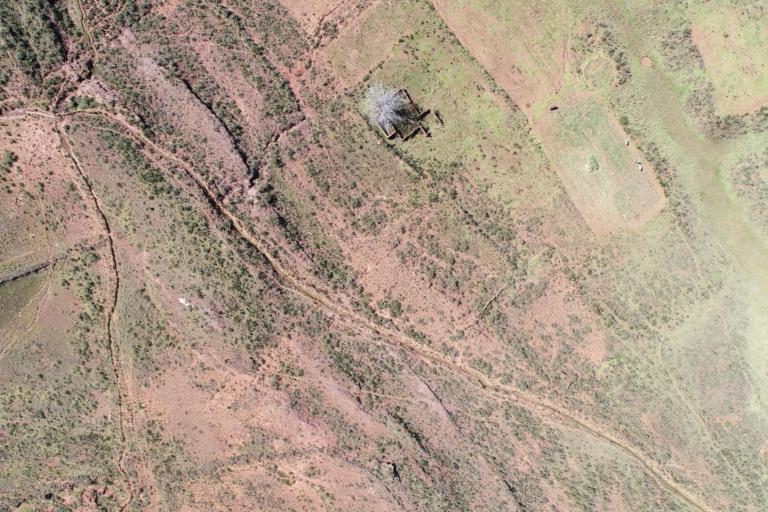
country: BO
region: La Paz
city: Tiahuanaco
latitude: -16.6071
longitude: -68.7760
